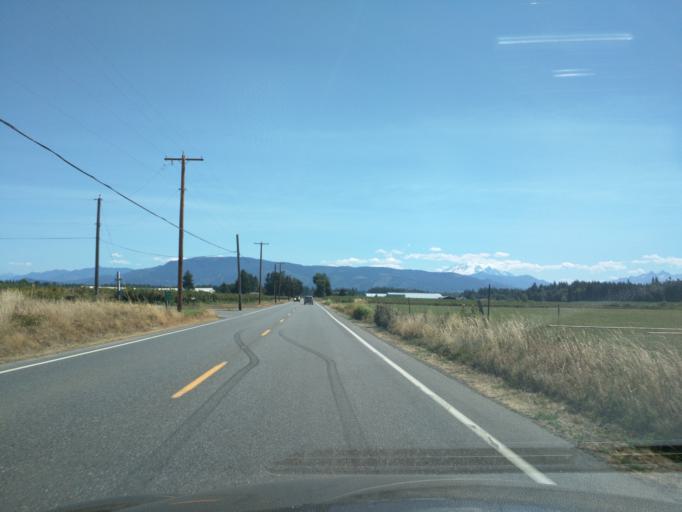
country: US
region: Washington
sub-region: Whatcom County
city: Lynden
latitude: 48.8917
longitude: -122.4208
